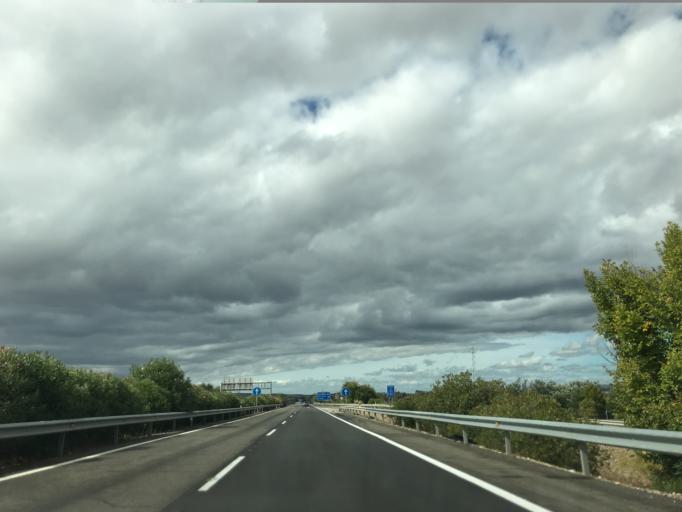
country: ES
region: Andalusia
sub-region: Province of Cordoba
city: Villa del Rio
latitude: 37.9870
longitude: -4.2817
